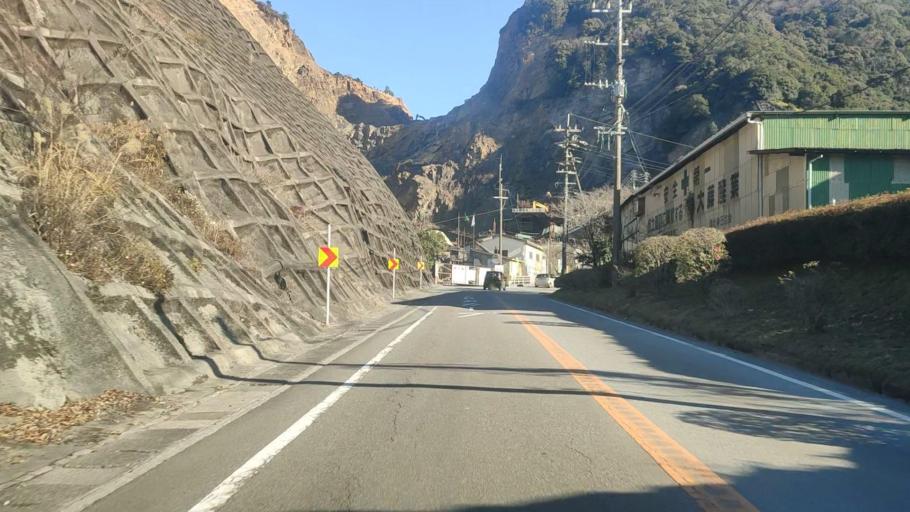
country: JP
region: Miyazaki
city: Nobeoka
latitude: 32.6280
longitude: 131.7171
